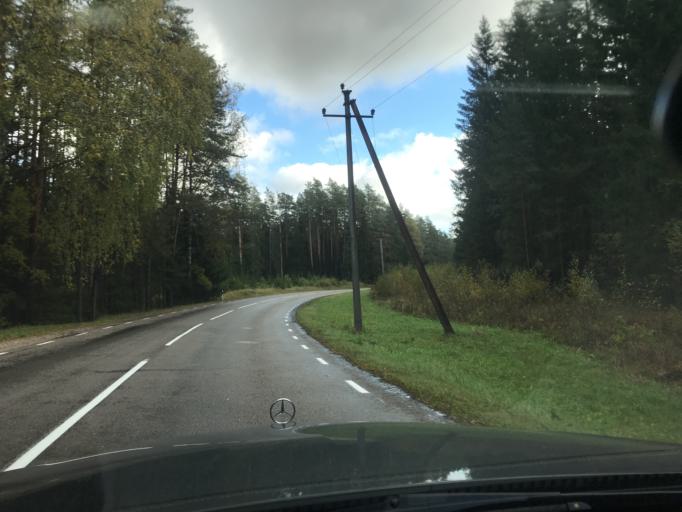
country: EE
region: Valgamaa
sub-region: Torva linn
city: Torva
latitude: 58.0113
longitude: 26.1108
